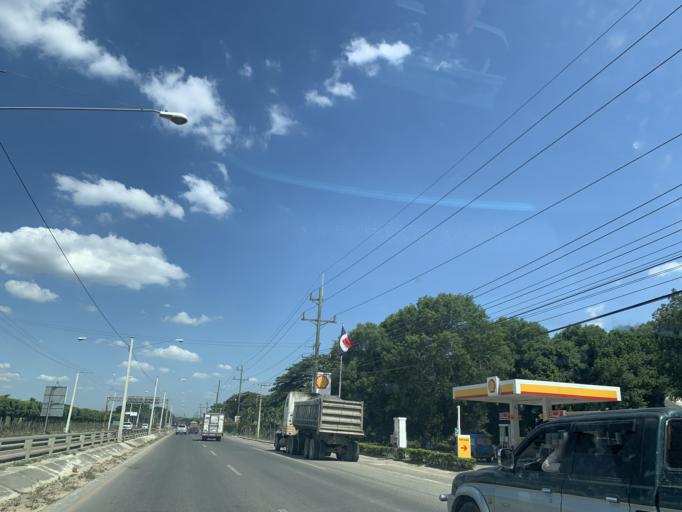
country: DO
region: Santiago
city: Villa Bisono
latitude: 19.5530
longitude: -70.8587
